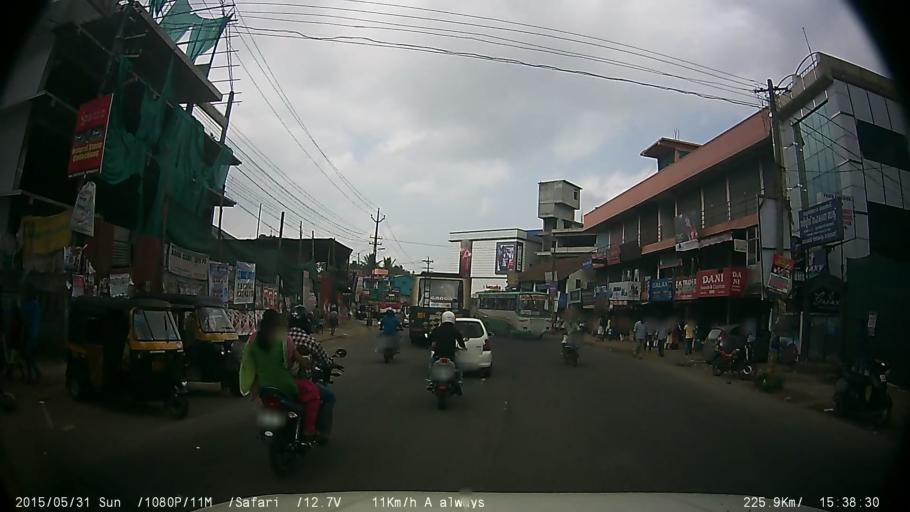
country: IN
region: Kerala
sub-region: Wayanad
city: Panamaram
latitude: 11.6639
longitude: 76.2614
